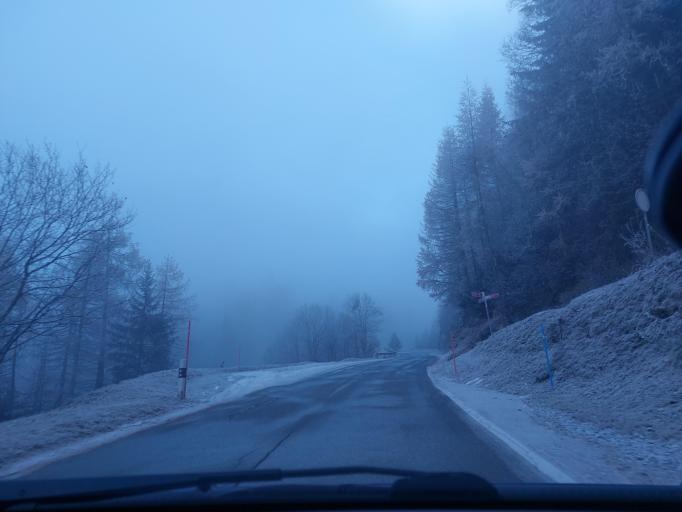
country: CH
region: Valais
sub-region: Conthey District
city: Basse-Nendaz
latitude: 46.1424
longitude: 7.3161
